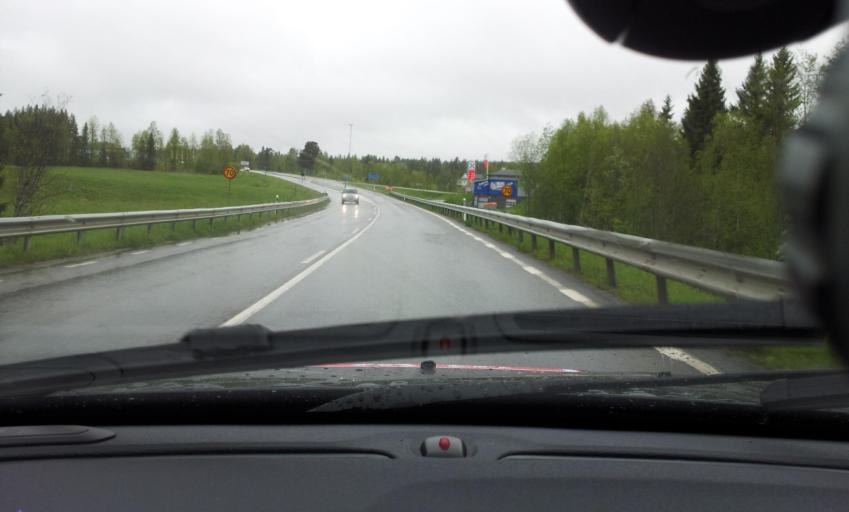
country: SE
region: Jaemtland
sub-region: Bergs Kommun
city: Hoverberg
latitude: 62.7535
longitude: 14.4307
